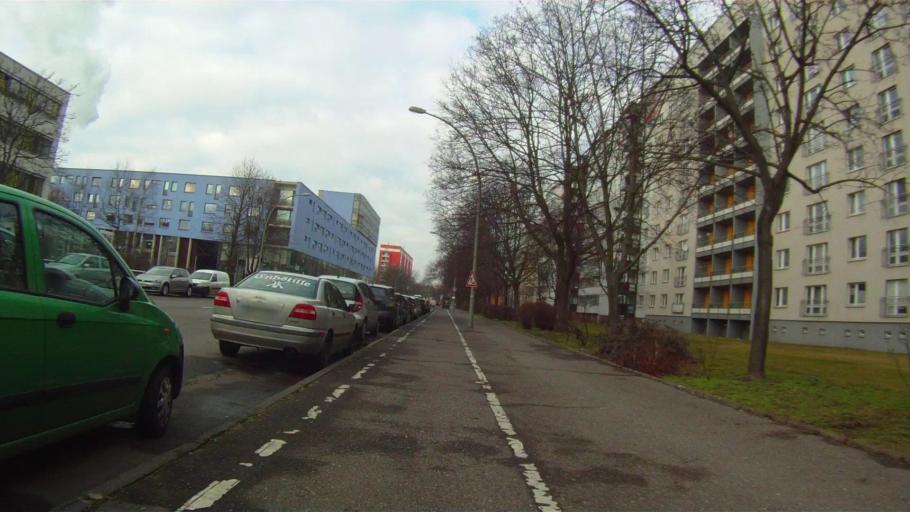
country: DE
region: Berlin
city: Friedrichsfelde
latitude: 52.4961
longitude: 13.5121
